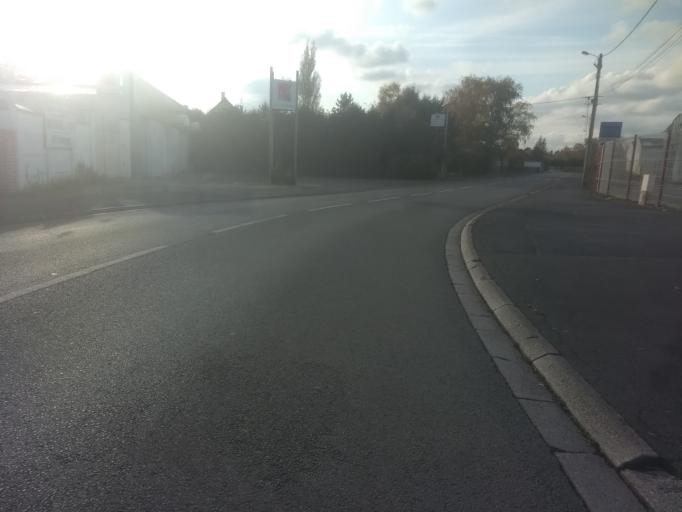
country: FR
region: Nord-Pas-de-Calais
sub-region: Departement du Pas-de-Calais
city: Achicourt
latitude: 50.2740
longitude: 2.7689
